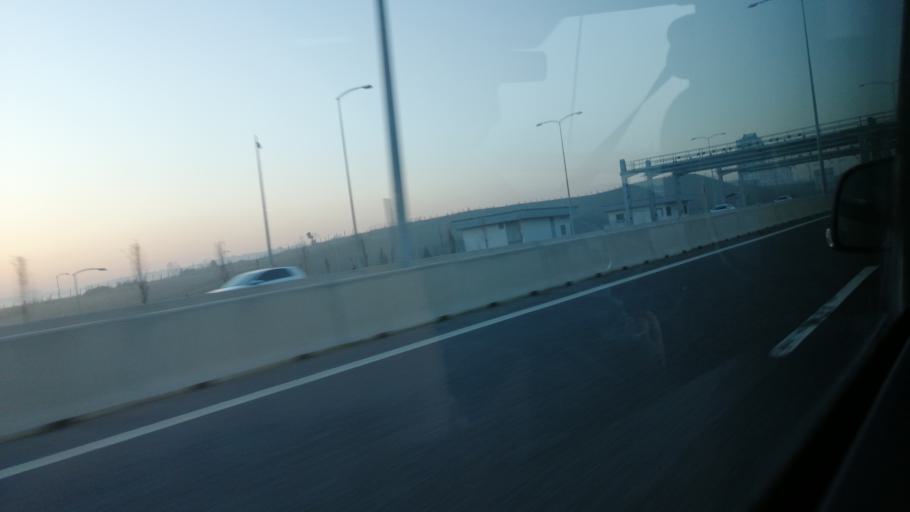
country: TR
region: Kocaeli
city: Tavsanli
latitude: 40.7843
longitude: 29.5161
